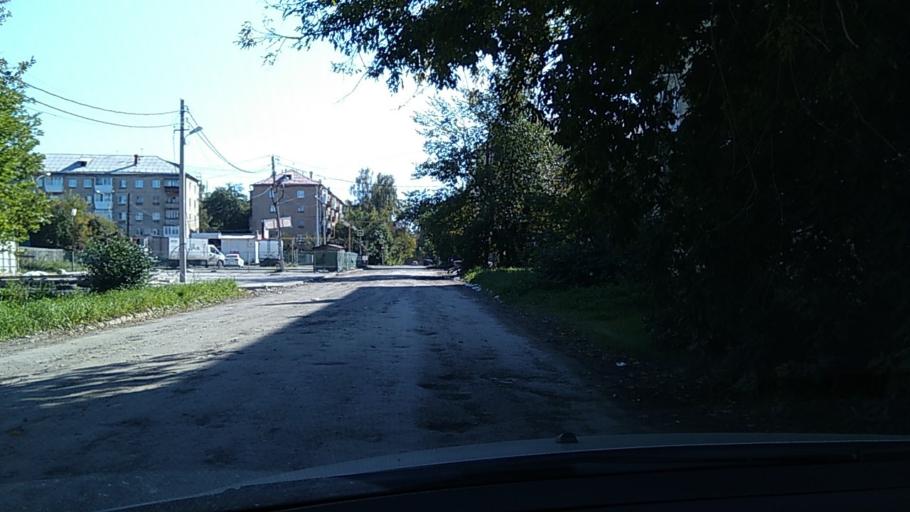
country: RU
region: Sverdlovsk
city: Yekaterinburg
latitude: 56.8885
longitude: 60.5646
